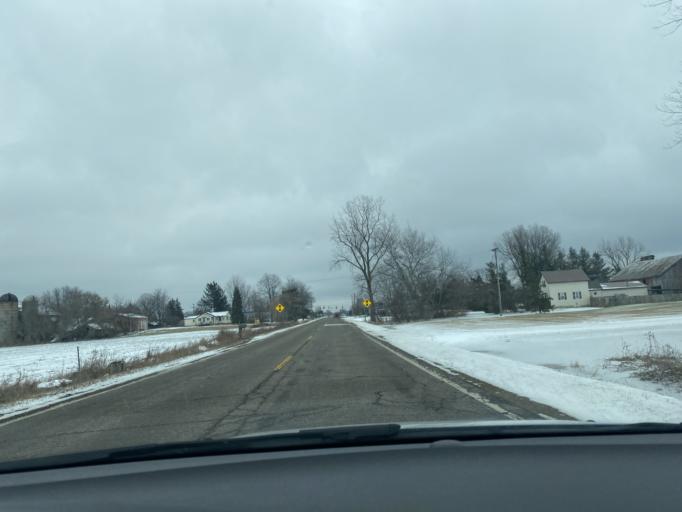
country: US
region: Michigan
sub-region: Sanilac County
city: Brown City
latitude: 43.2105
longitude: -83.0809
